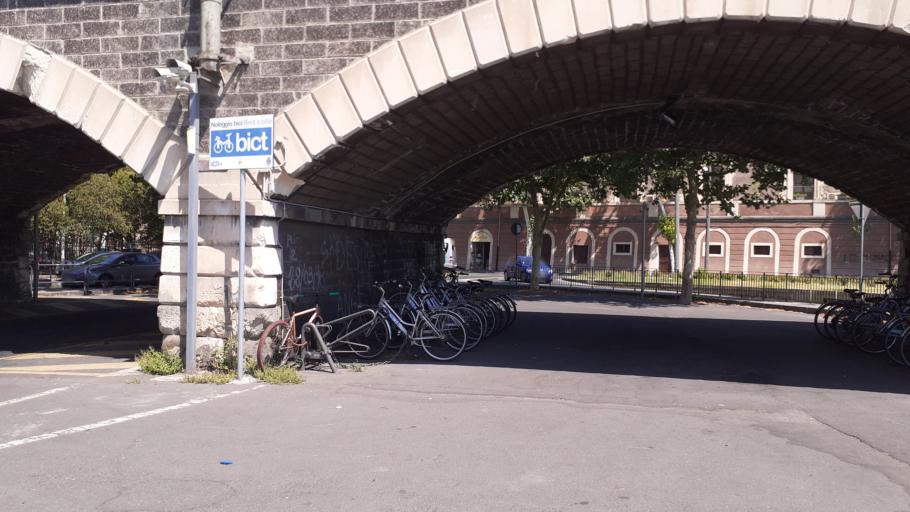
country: IT
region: Sicily
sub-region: Catania
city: Catania
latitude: 37.5014
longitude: 15.0891
